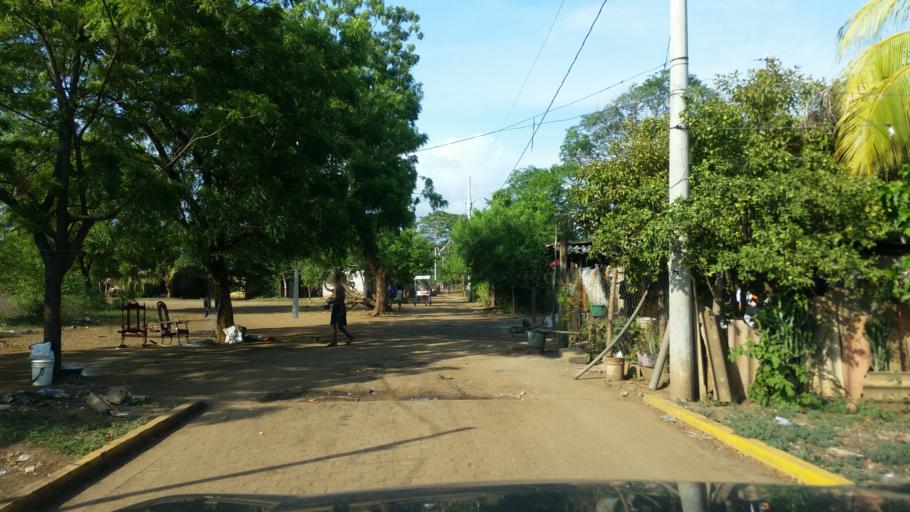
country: NI
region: Managua
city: Masachapa
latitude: 11.7892
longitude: -86.5126
